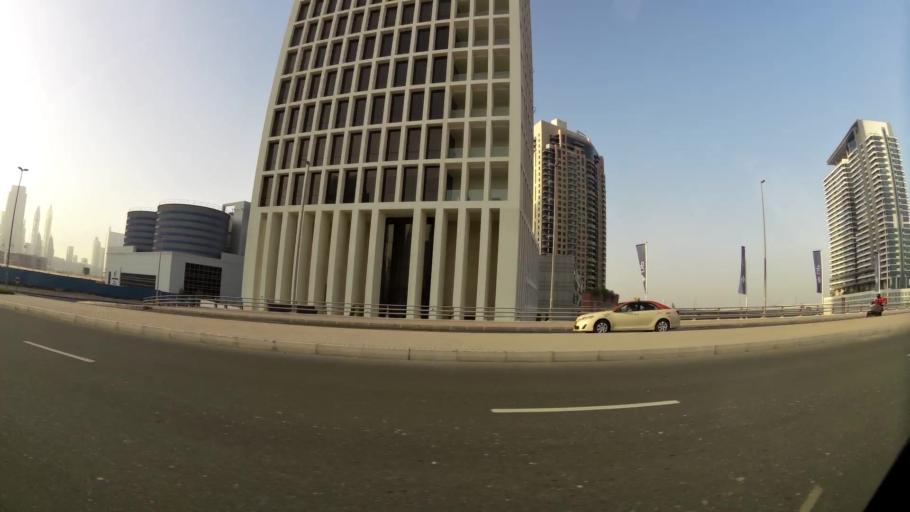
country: AE
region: Dubai
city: Dubai
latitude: 25.1916
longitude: 55.2882
